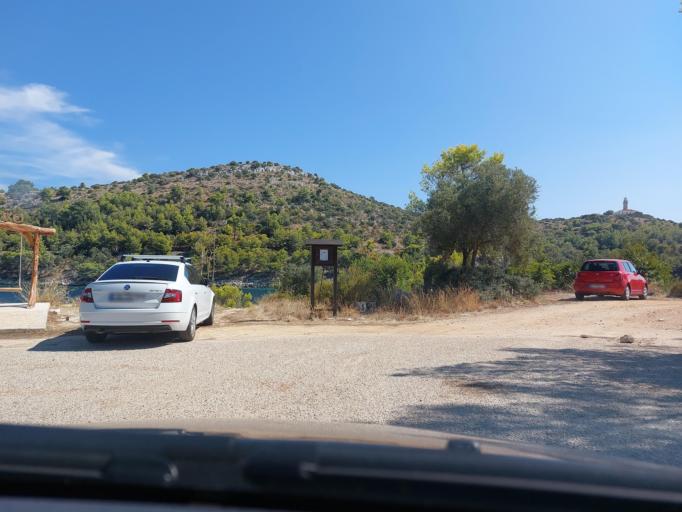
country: HR
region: Dubrovacko-Neretvanska
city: Smokvica
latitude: 42.7308
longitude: 16.8858
